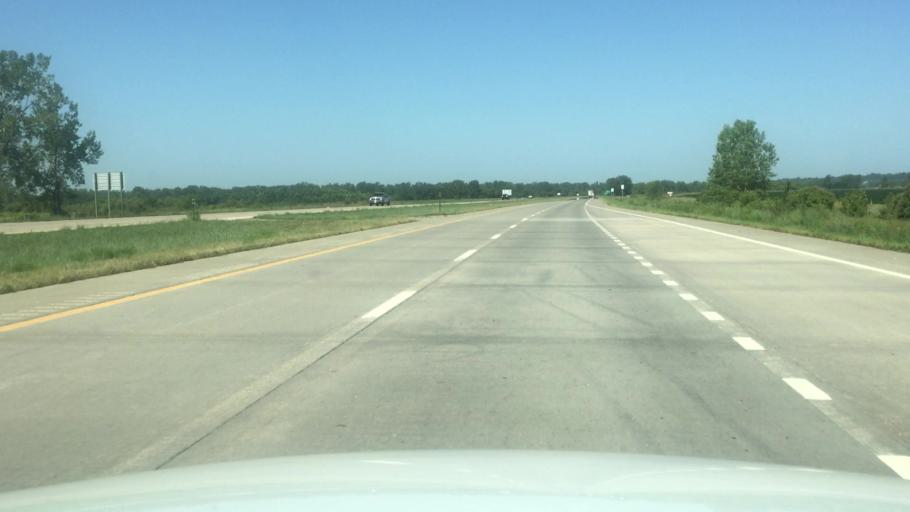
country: US
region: Kansas
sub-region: Doniphan County
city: Elwood
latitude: 39.7407
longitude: -94.8993
